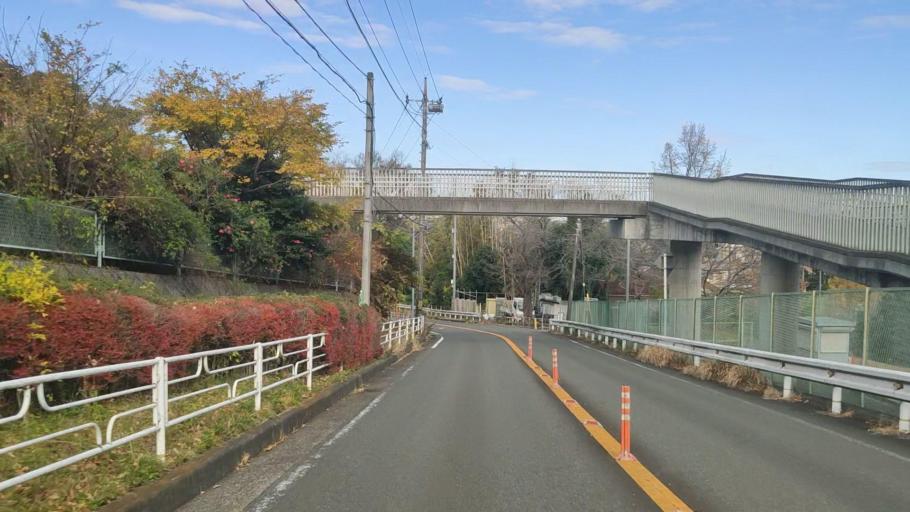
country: JP
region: Kanagawa
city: Minami-rinkan
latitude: 35.4528
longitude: 139.5393
